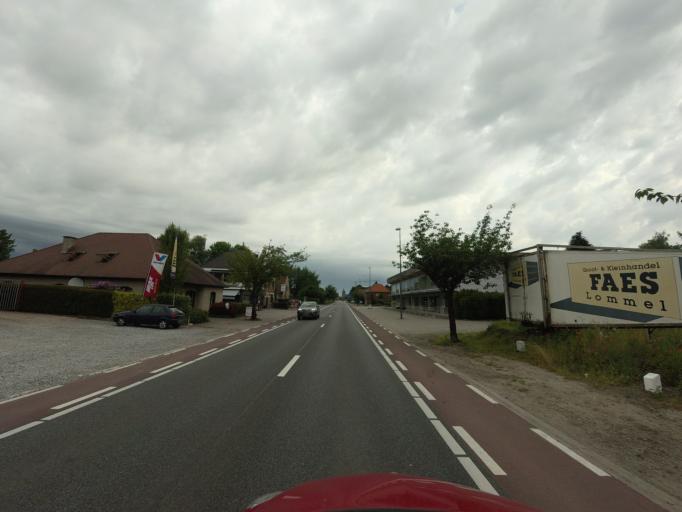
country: BE
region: Flanders
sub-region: Provincie Limburg
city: Lommel
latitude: 51.2183
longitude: 5.3135
